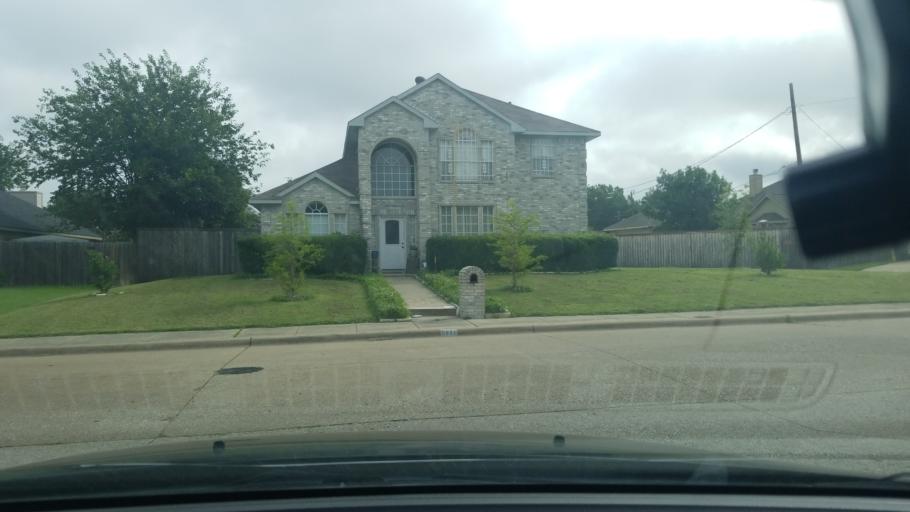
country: US
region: Texas
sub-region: Dallas County
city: Balch Springs
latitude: 32.7865
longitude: -96.6898
